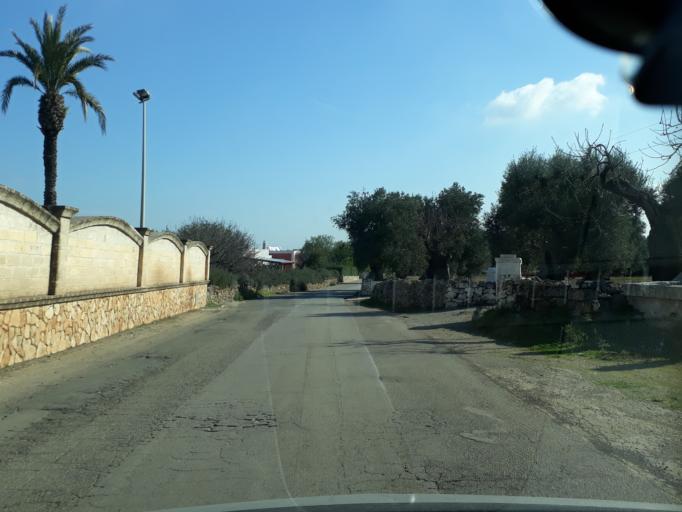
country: IT
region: Apulia
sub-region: Provincia di Brindisi
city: Fasano
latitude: 40.8259
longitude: 17.3792
